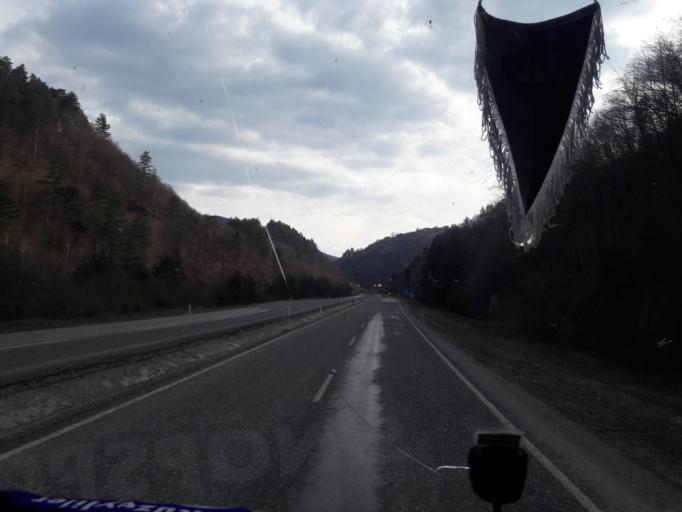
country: TR
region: Kastamonu
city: Kuzyaka
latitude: 41.1476
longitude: 33.7827
